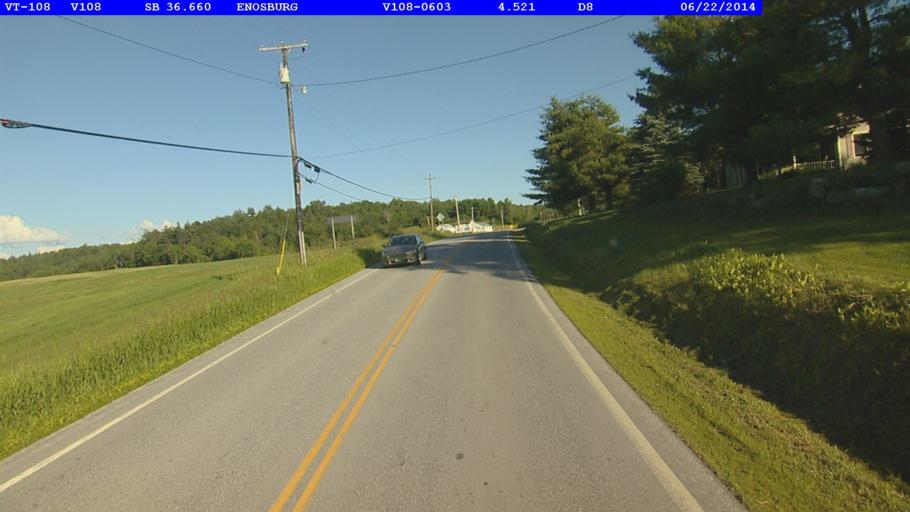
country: US
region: Vermont
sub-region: Franklin County
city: Enosburg Falls
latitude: 44.8999
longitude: -72.8029
